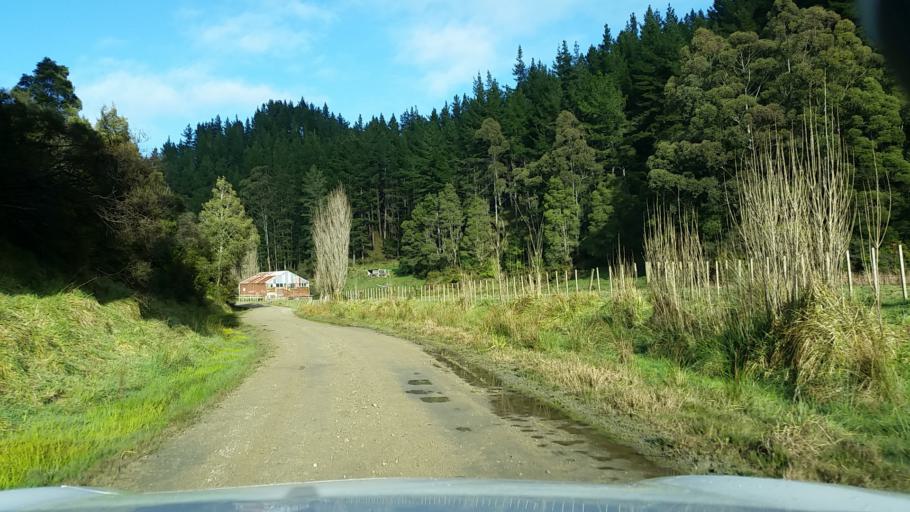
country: NZ
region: Taranaki
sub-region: South Taranaki District
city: Patea
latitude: -39.6740
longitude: 174.7652
